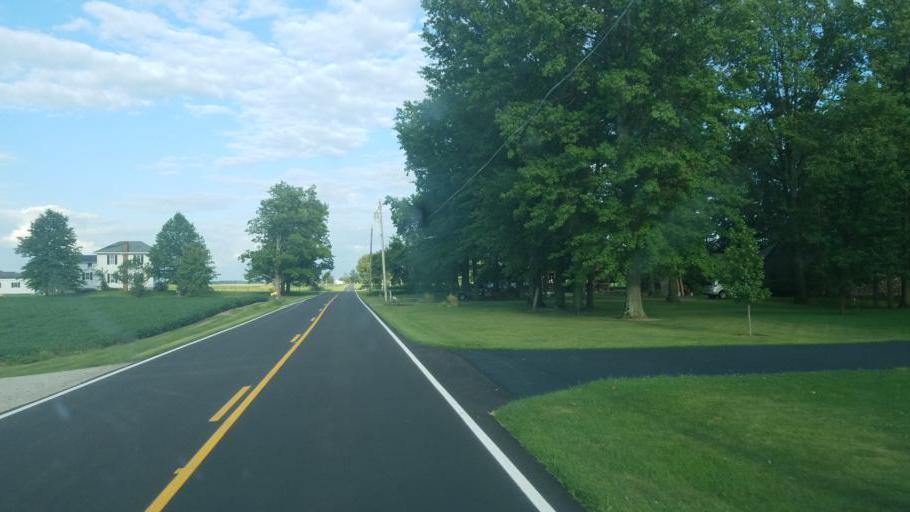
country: US
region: Ohio
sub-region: Seneca County
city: Tiffin
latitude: 41.1100
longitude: -83.0847
